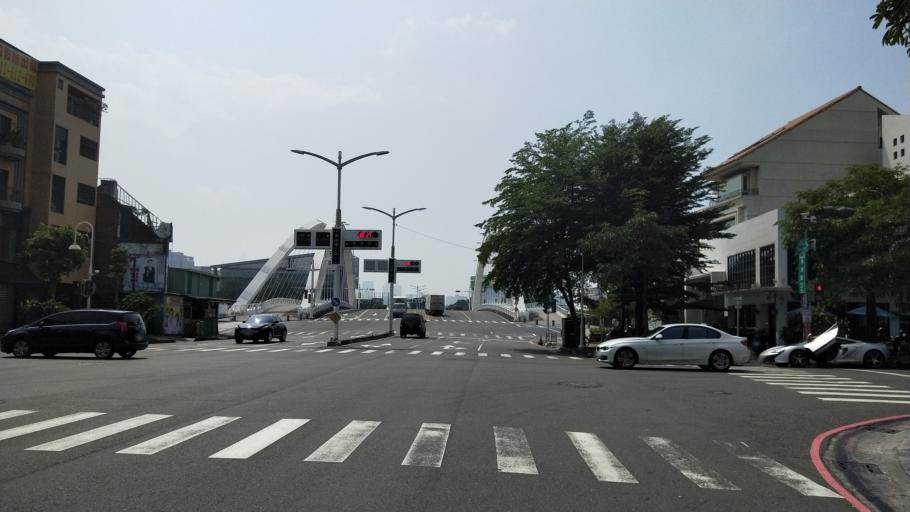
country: TW
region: Kaohsiung
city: Kaohsiung
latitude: 22.6517
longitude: 120.2879
